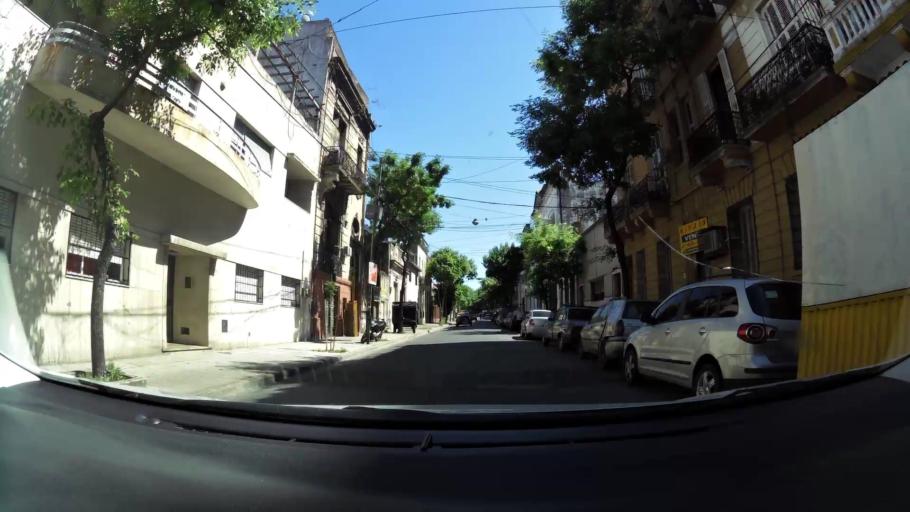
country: AR
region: Buenos Aires F.D.
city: Buenos Aires
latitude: -34.6257
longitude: -58.3871
